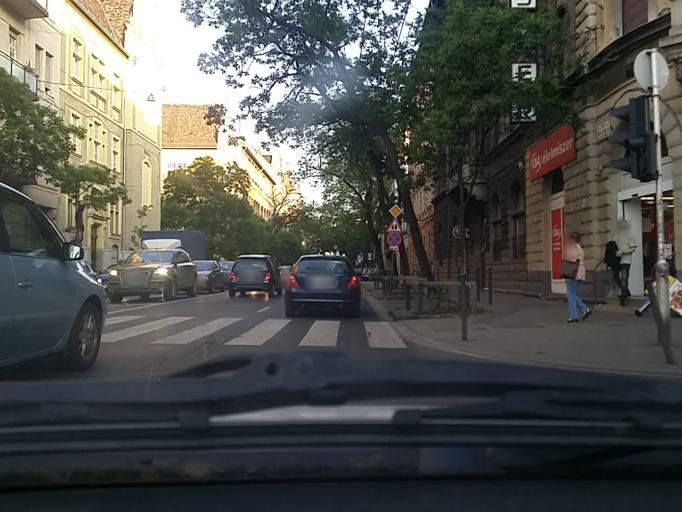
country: HU
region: Budapest
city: Budapest VII. keruelet
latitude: 47.5067
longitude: 19.0857
